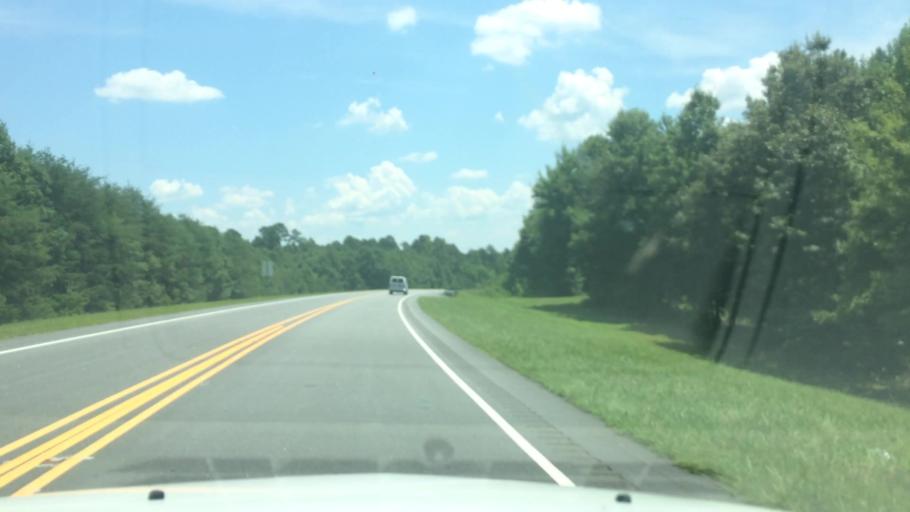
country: US
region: North Carolina
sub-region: Alexander County
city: Stony Point
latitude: 35.8864
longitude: -81.0790
